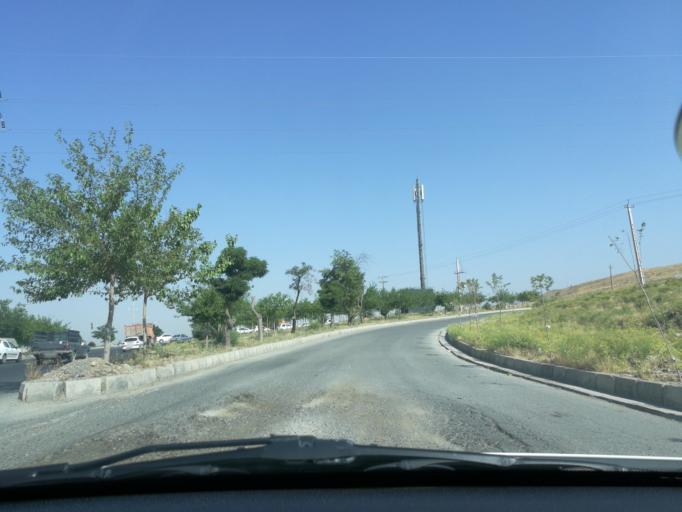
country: IR
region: Alborz
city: Karaj
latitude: 35.8650
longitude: 50.9282
